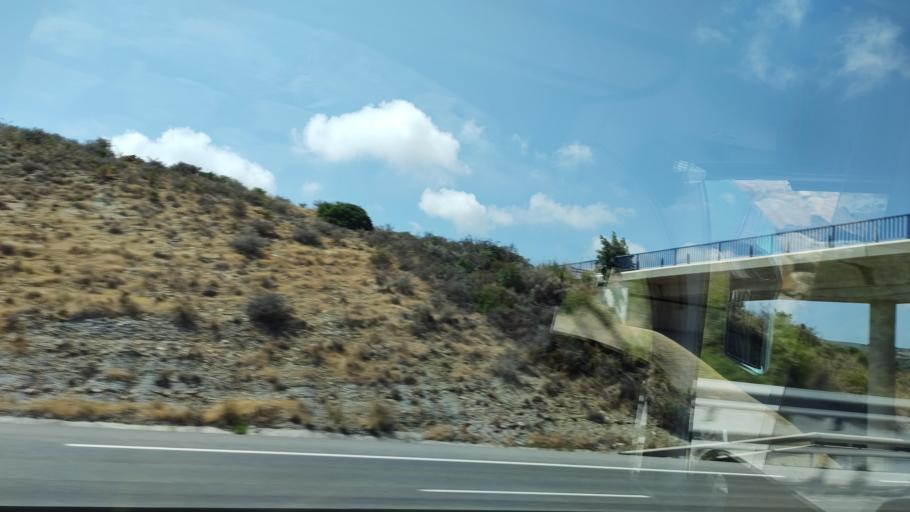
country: ES
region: Andalusia
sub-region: Provincia de Malaga
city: Manilva
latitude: 36.3536
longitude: -5.2705
